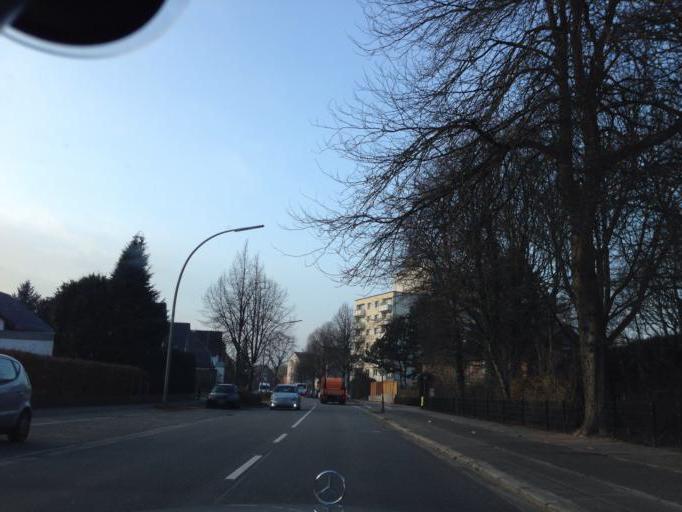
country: DE
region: Schleswig-Holstein
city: Barsbuettel
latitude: 53.6040
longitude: 10.1778
